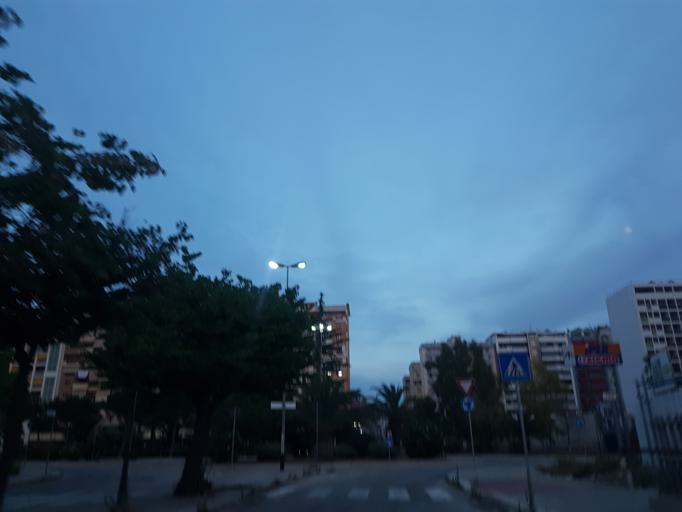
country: IT
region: Apulia
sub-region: Provincia di Barletta - Andria - Trani
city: Barletta
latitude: 41.3058
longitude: 16.2768
